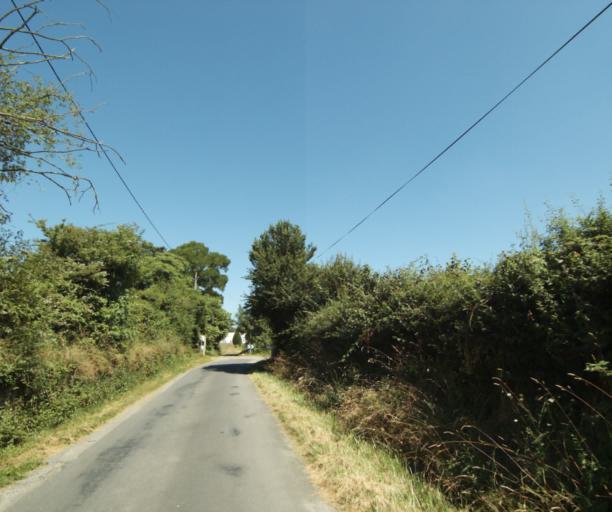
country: FR
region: Pays de la Loire
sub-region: Departement de la Mayenne
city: Laval
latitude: 48.0703
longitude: -0.7456
